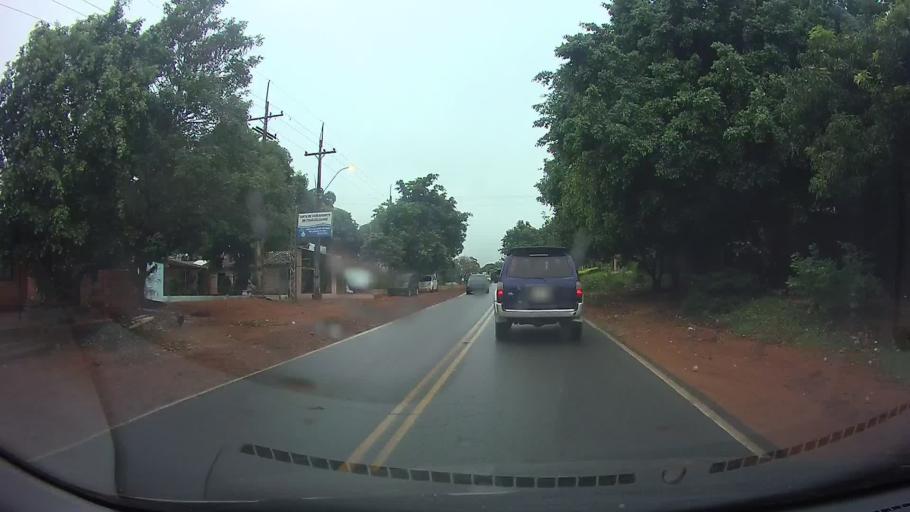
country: PY
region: Central
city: Ita
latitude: -25.4395
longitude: -57.3682
